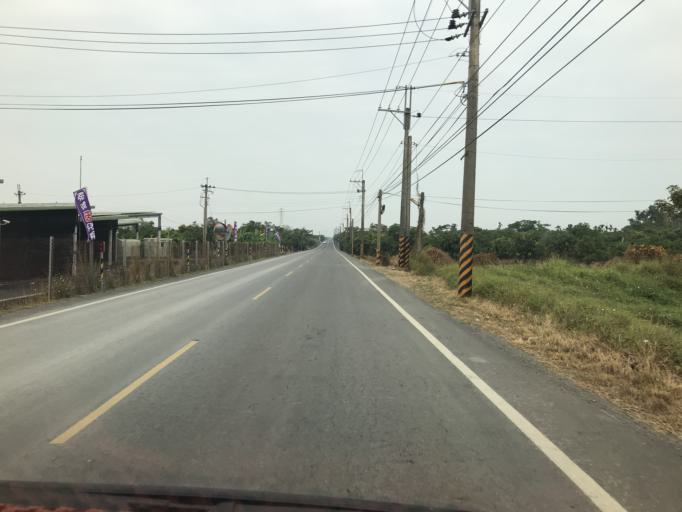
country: TW
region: Taiwan
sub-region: Pingtung
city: Pingtung
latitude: 22.4588
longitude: 120.6134
